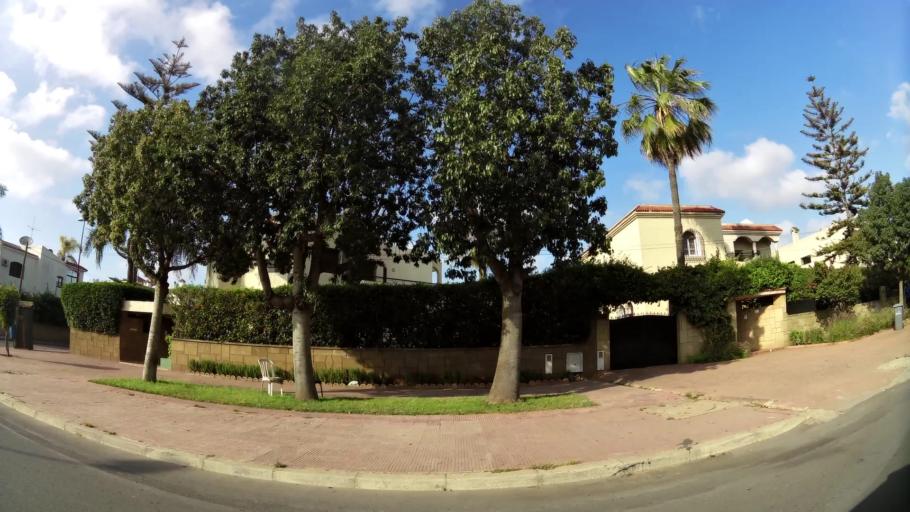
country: MA
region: Rabat-Sale-Zemmour-Zaer
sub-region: Skhirate-Temara
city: Temara
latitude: 33.9561
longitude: -6.8583
